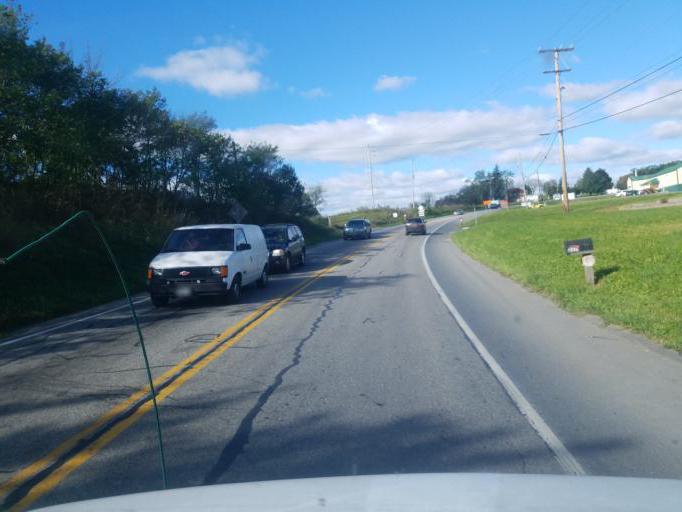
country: US
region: Pennsylvania
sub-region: Franklin County
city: Greencastle
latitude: 39.7917
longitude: -77.7554
